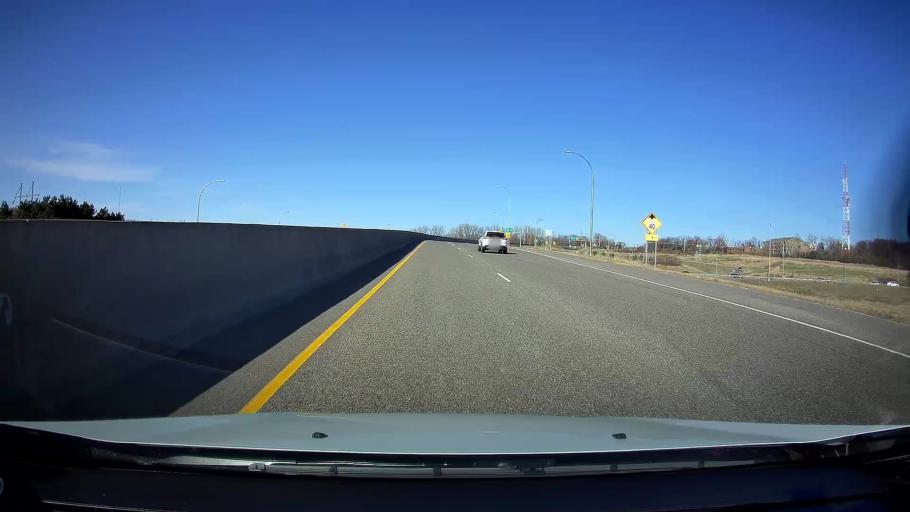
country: US
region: Minnesota
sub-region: Ramsey County
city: Arden Hills
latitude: 45.0598
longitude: -93.1573
